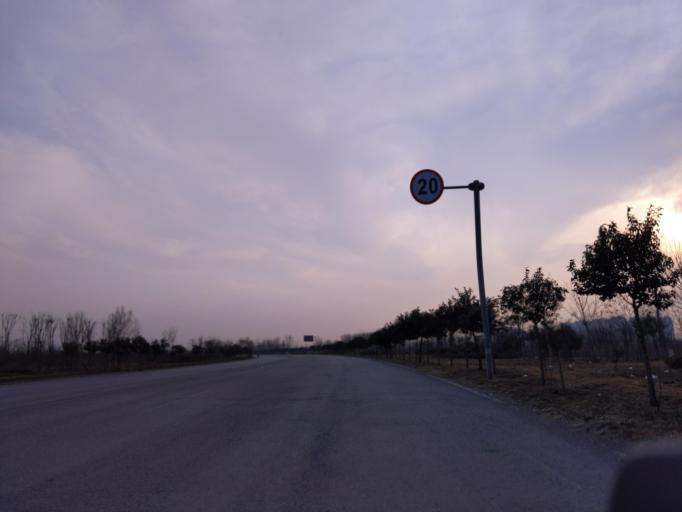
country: CN
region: Henan Sheng
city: Puyang
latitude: 35.8167
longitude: 114.9693
